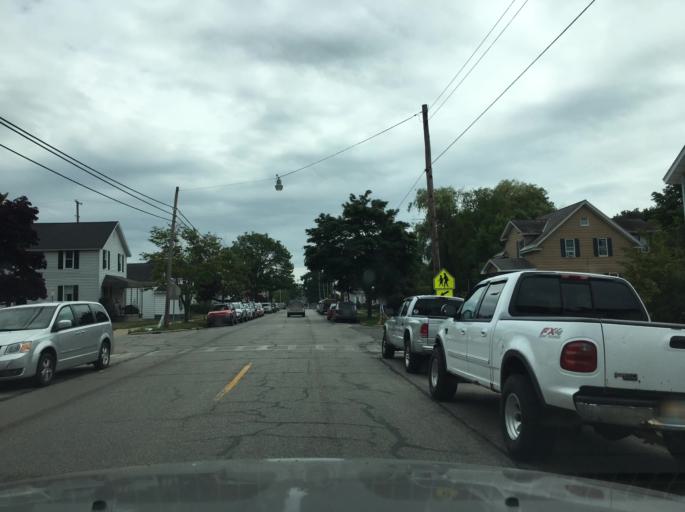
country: US
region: Michigan
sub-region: Mason County
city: Ludington
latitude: 43.9538
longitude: -86.4395
